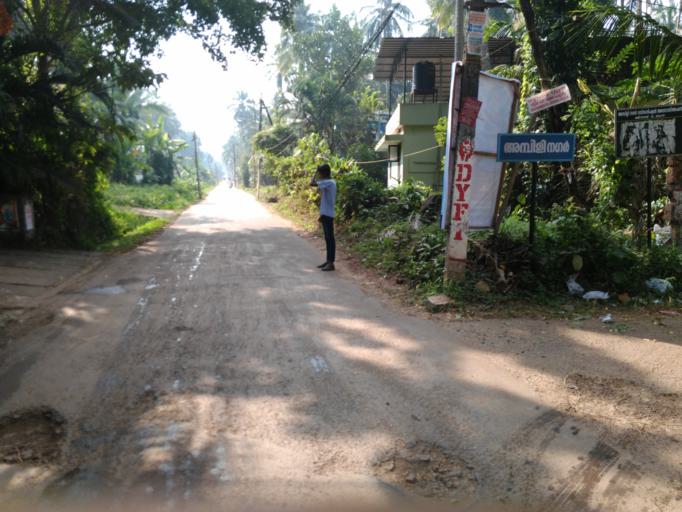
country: IN
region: Kerala
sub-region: Kozhikode
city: Kunnamangalam
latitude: 11.2888
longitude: 75.8227
